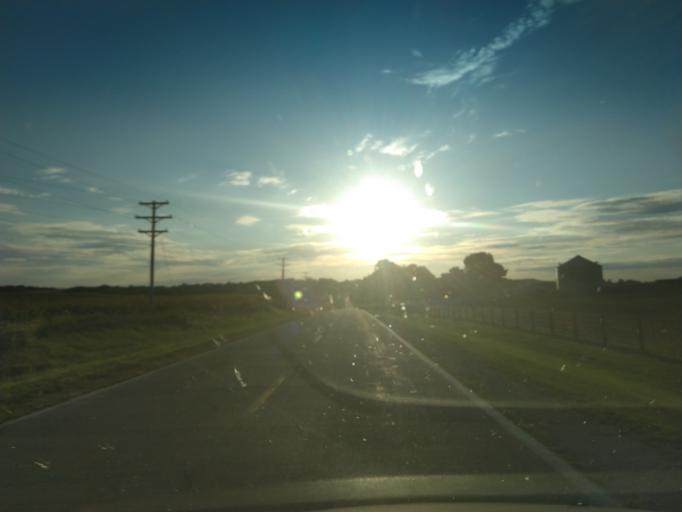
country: US
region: Iowa
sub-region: Jackson County
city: Maquoketa
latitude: 42.1644
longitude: -90.7193
